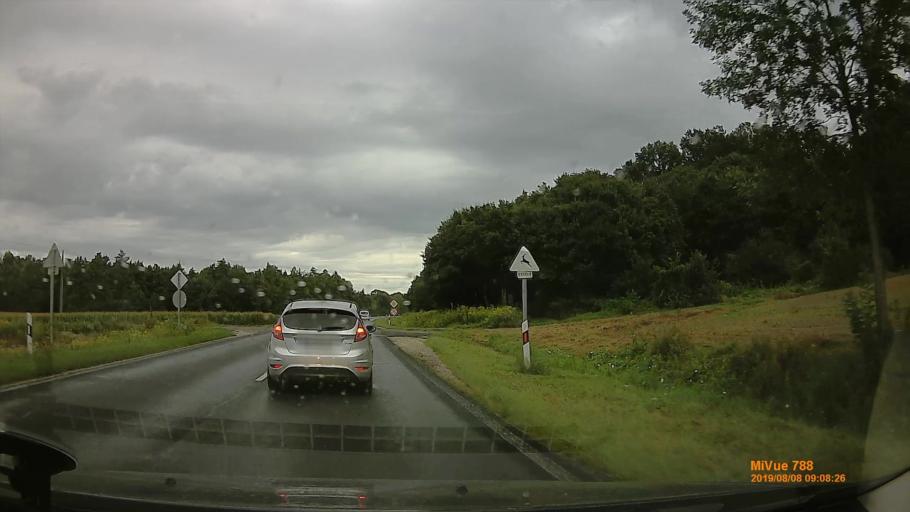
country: HU
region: Zala
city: Zalaegerszeg
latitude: 46.7457
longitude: 16.8551
